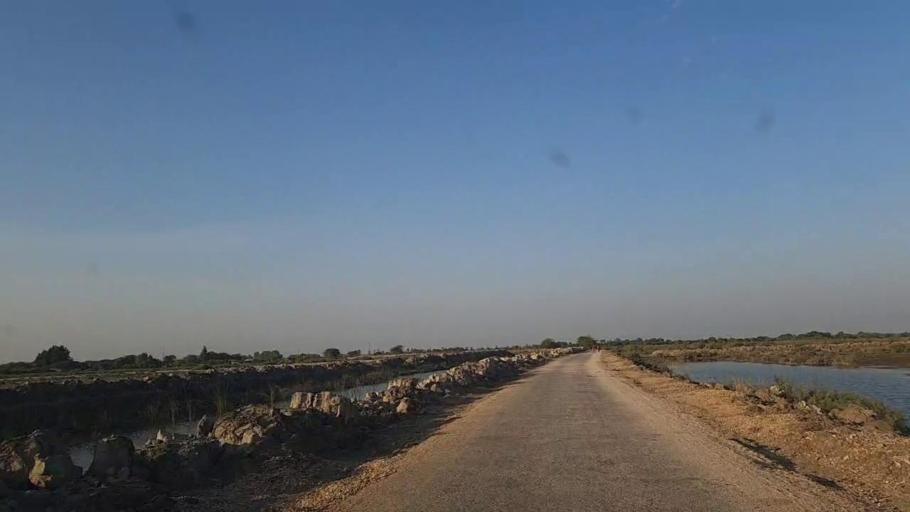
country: PK
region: Sindh
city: Mirpur Batoro
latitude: 24.6940
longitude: 68.2002
